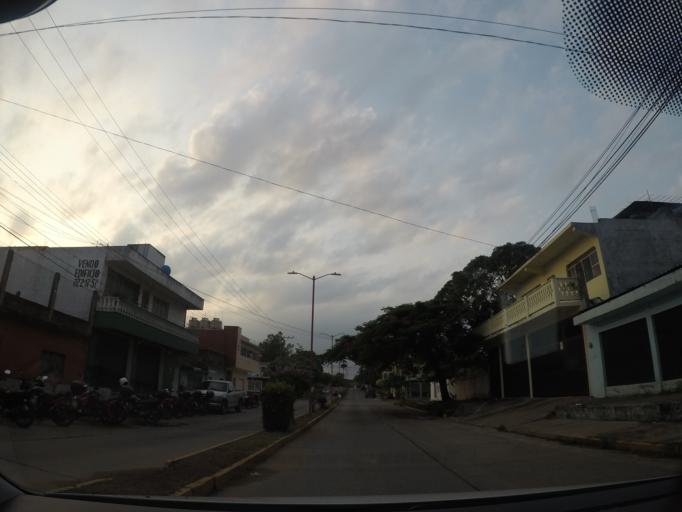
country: MX
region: Oaxaca
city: Matias Romero
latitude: 16.8756
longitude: -95.0383
